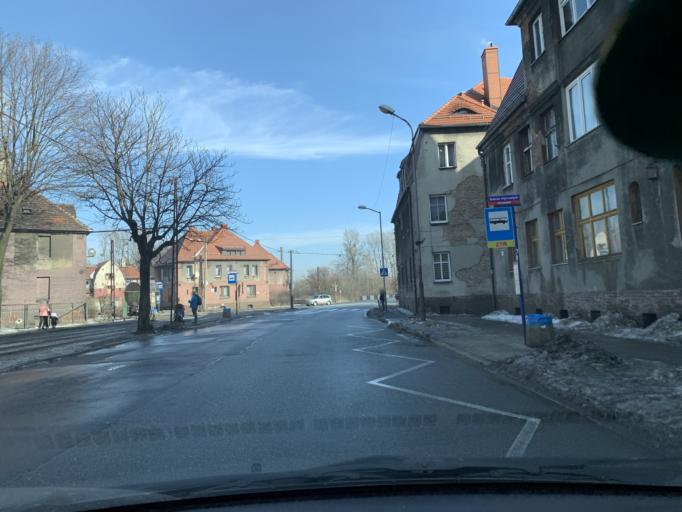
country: PL
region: Silesian Voivodeship
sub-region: Bytom
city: Bytom
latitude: 50.3388
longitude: 18.8729
